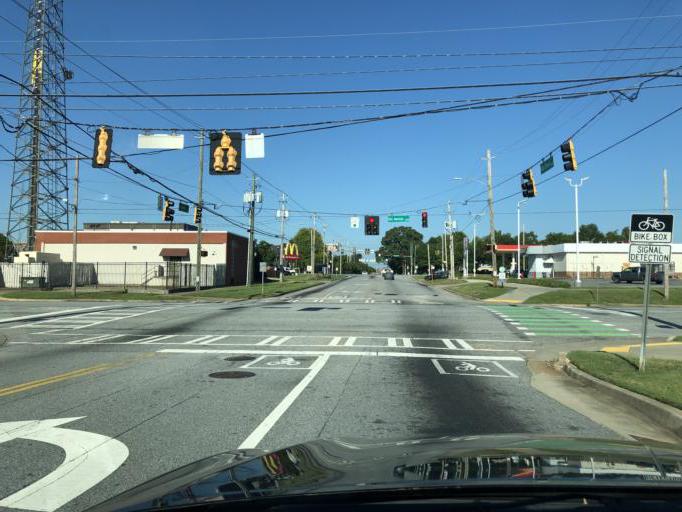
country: US
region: Georgia
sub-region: Muscogee County
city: Columbus
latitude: 32.4724
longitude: -84.9861
